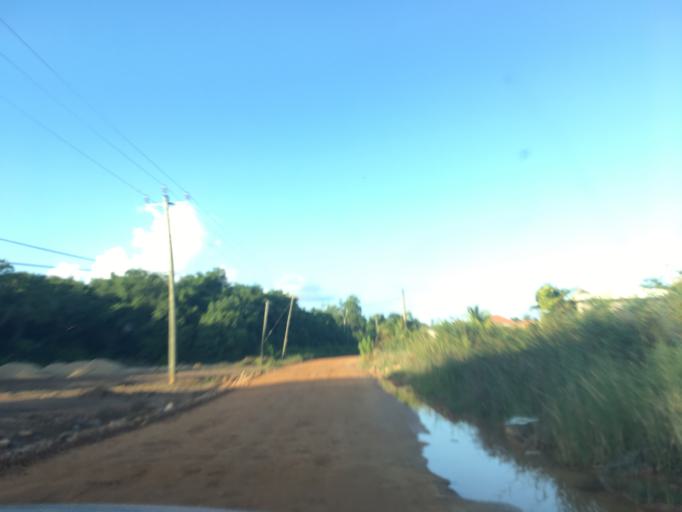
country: BZ
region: Stann Creek
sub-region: Dangriga
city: Dangriga
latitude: 16.8297
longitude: -88.2671
